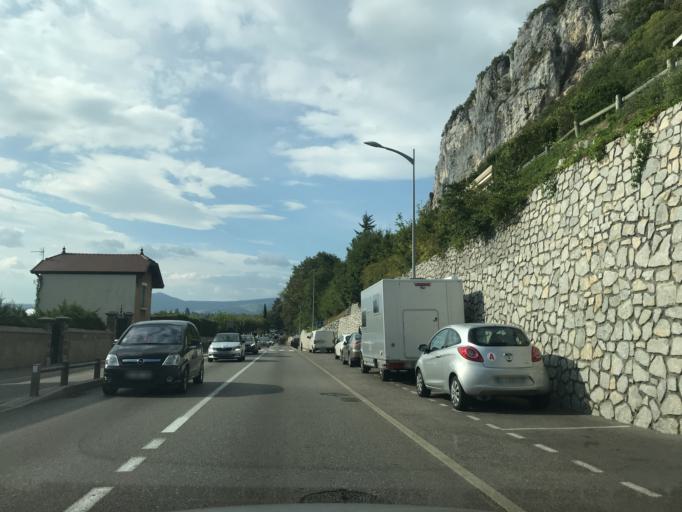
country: FR
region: Rhone-Alpes
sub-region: Departement de la Haute-Savoie
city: Veyrier-du-Lac
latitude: 45.8964
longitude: 6.1652
